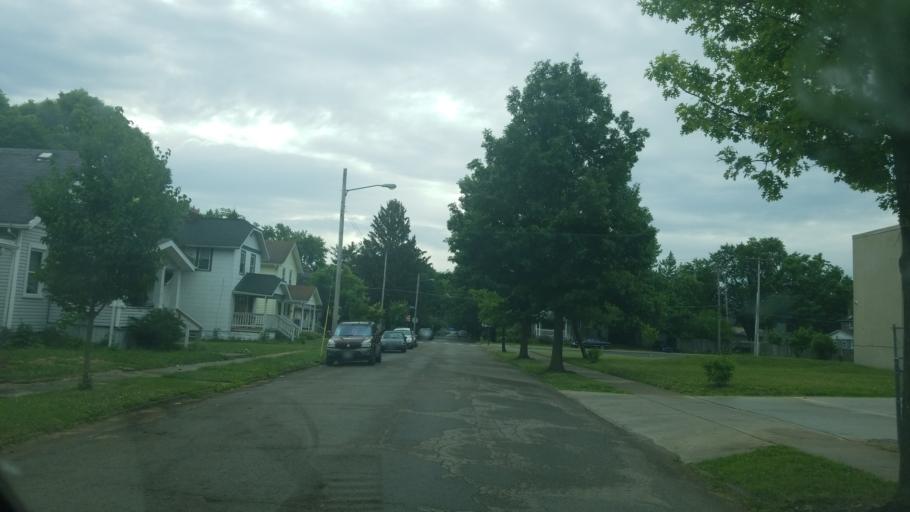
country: US
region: Ohio
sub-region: Franklin County
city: Bexley
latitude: 40.0181
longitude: -82.9732
